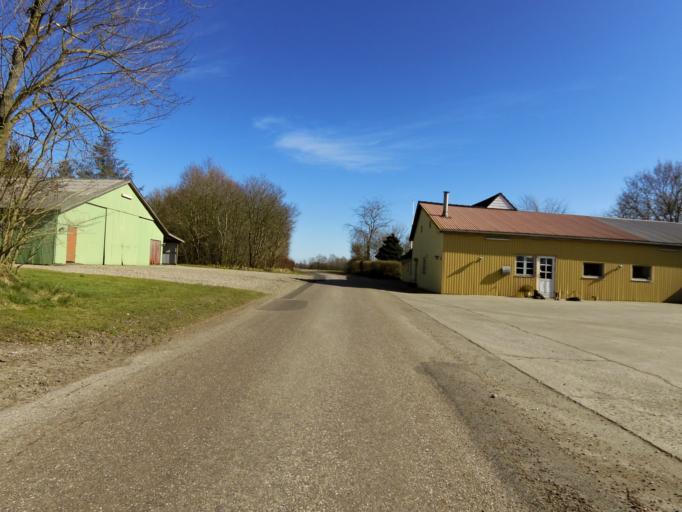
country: DK
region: South Denmark
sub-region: Tonder Kommune
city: Toftlund
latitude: 55.2361
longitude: 9.1122
